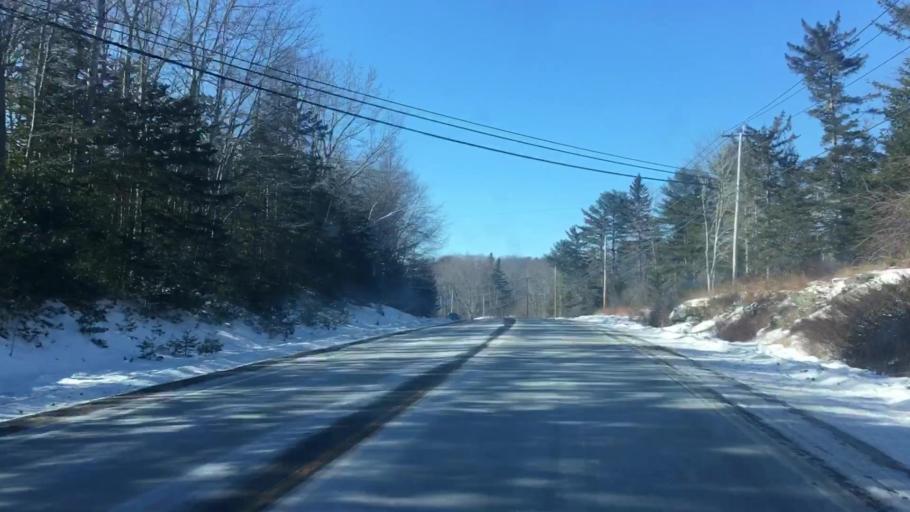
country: US
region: Maine
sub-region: Hancock County
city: Surry
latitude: 44.4947
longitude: -68.4695
